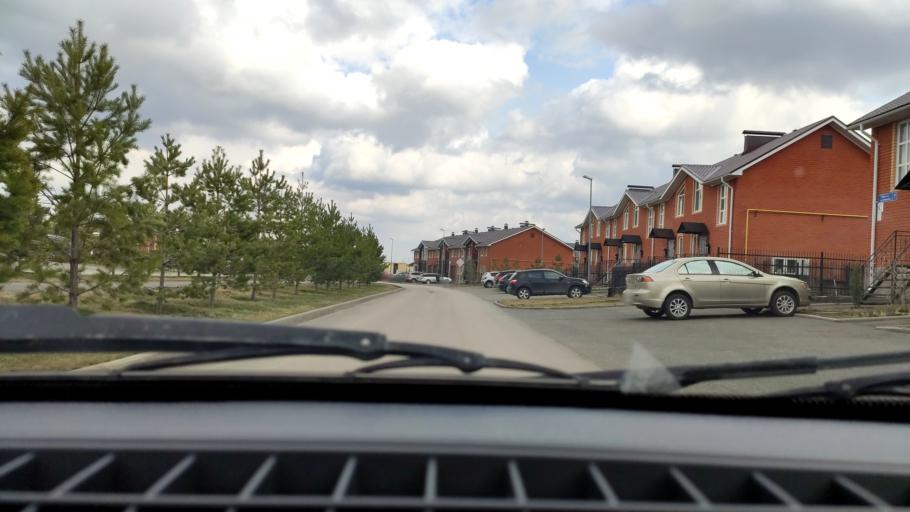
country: RU
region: Bashkortostan
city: Ufa
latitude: 54.5940
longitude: 55.9212
